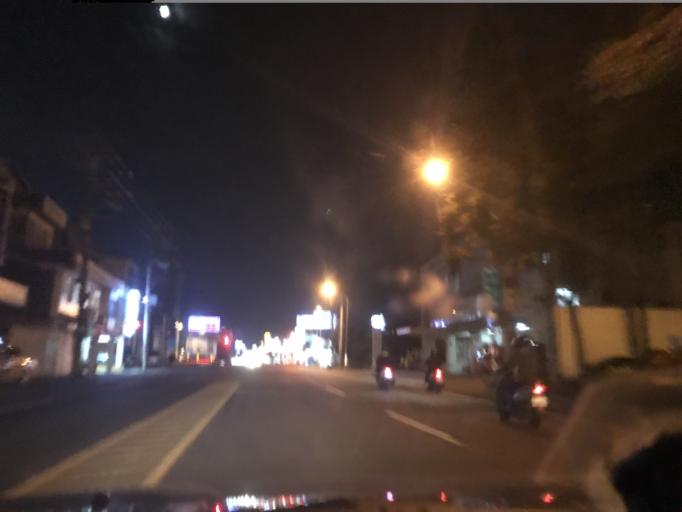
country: TW
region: Taiwan
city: Daxi
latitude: 24.8701
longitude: 121.2222
